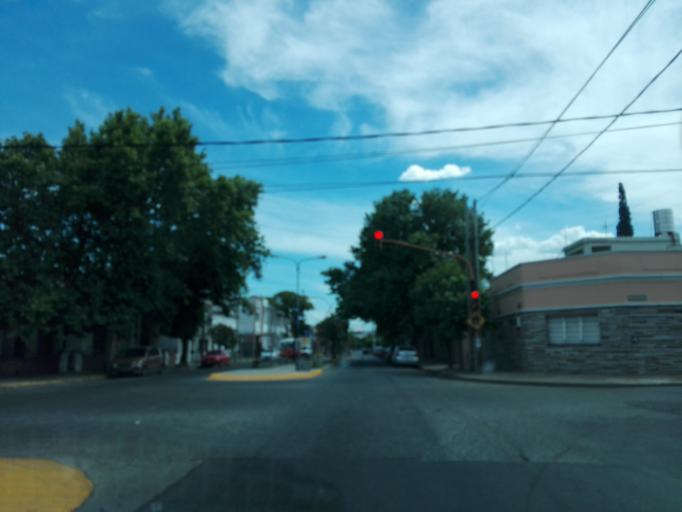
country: AR
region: Buenos Aires
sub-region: Partido de Lanus
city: Lanus
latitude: -34.7137
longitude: -58.3798
